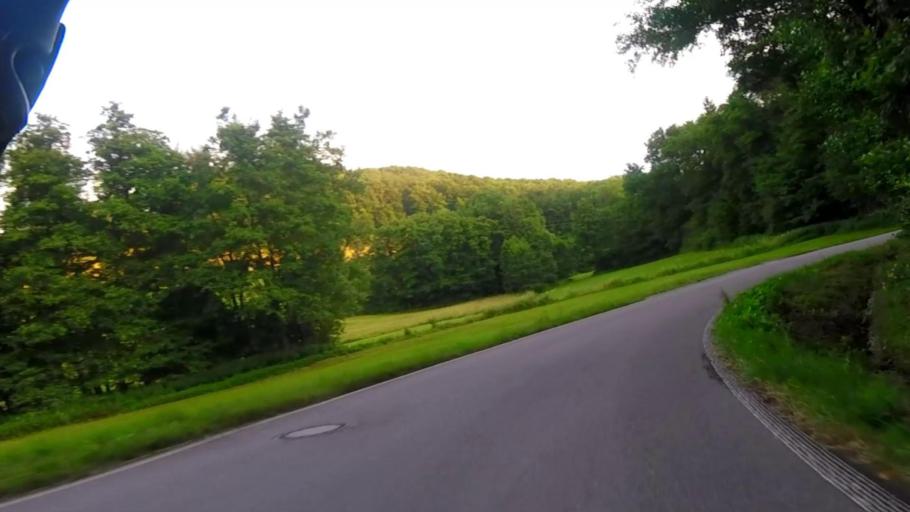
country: DE
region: Baden-Wuerttemberg
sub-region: Regierungsbezirk Stuttgart
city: Oberstenfeld
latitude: 49.0068
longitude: 9.3683
